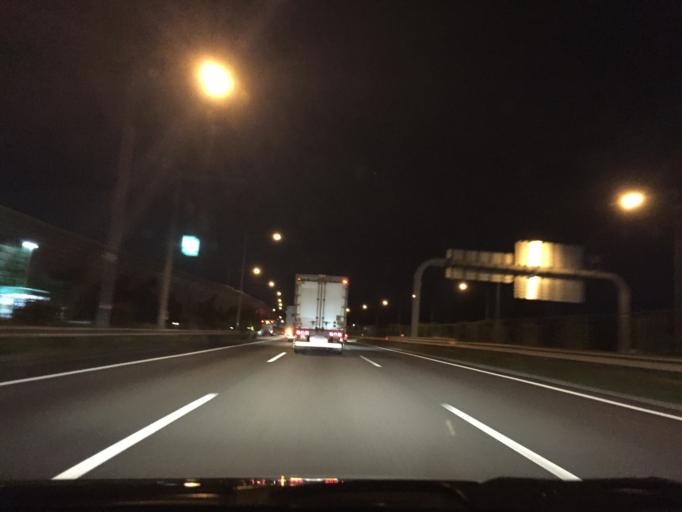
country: JP
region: Kanagawa
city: Atsugi
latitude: 35.4246
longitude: 139.3455
